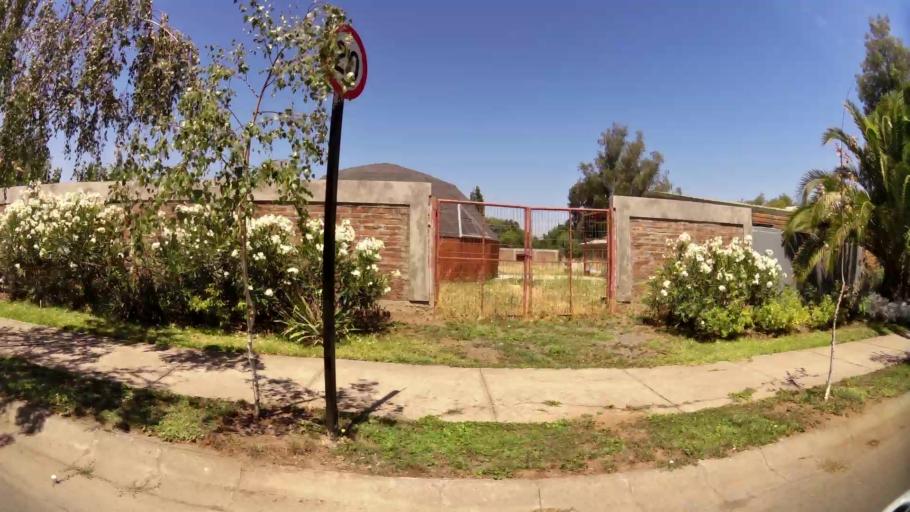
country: CL
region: Maule
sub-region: Provincia de Curico
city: Curico
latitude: -34.9893
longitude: -71.2281
